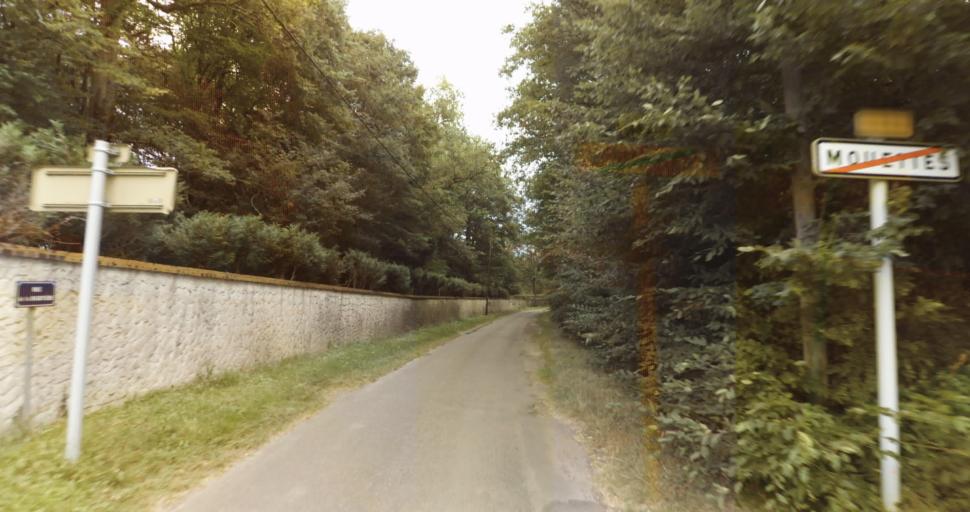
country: FR
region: Haute-Normandie
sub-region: Departement de l'Eure
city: La Couture-Boussey
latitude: 48.8979
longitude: 1.3615
